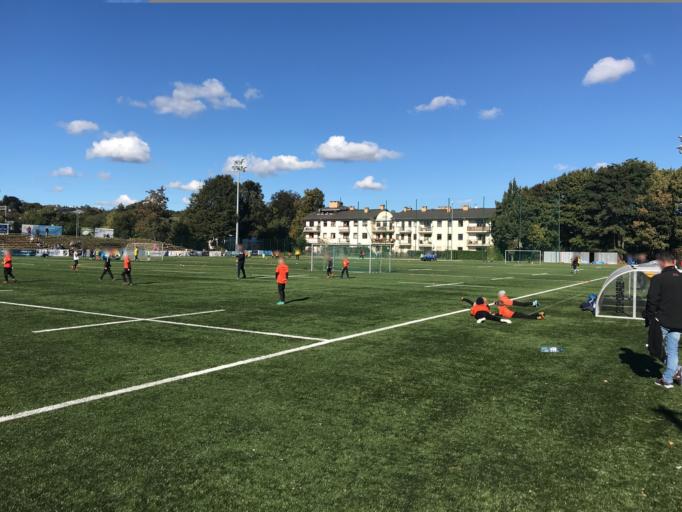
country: PL
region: Pomeranian Voivodeship
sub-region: Sopot
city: Sopot
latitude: 54.4333
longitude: 18.5667
